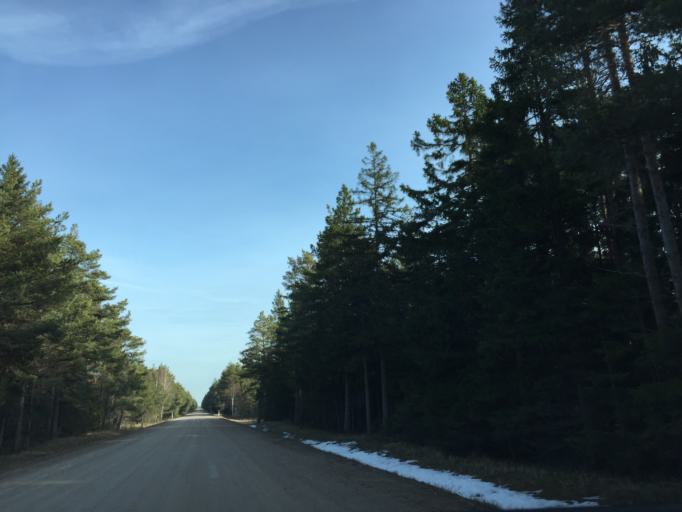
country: EE
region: Saare
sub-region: Kuressaare linn
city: Kuressaare
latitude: 58.3073
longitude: 21.9713
